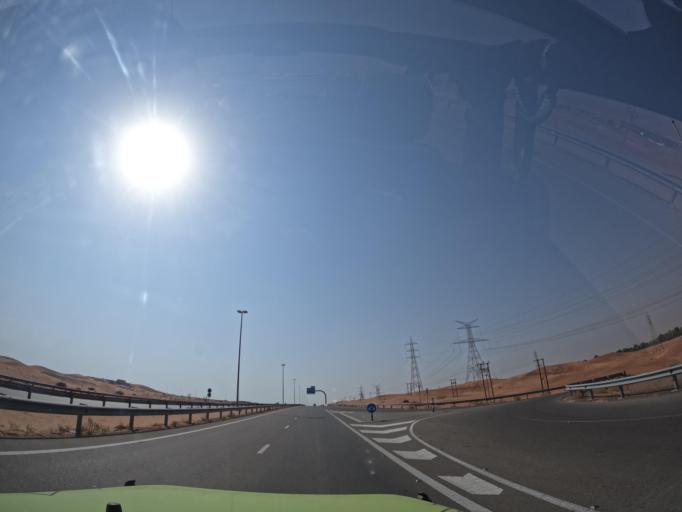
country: OM
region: Al Buraimi
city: Al Buraymi
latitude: 24.3503
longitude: 55.7370
